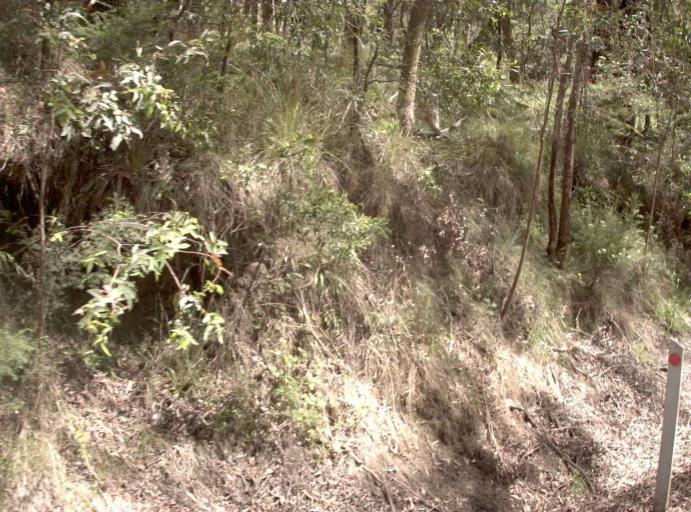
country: AU
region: Victoria
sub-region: East Gippsland
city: Lakes Entrance
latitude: -37.2266
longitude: 148.2634
